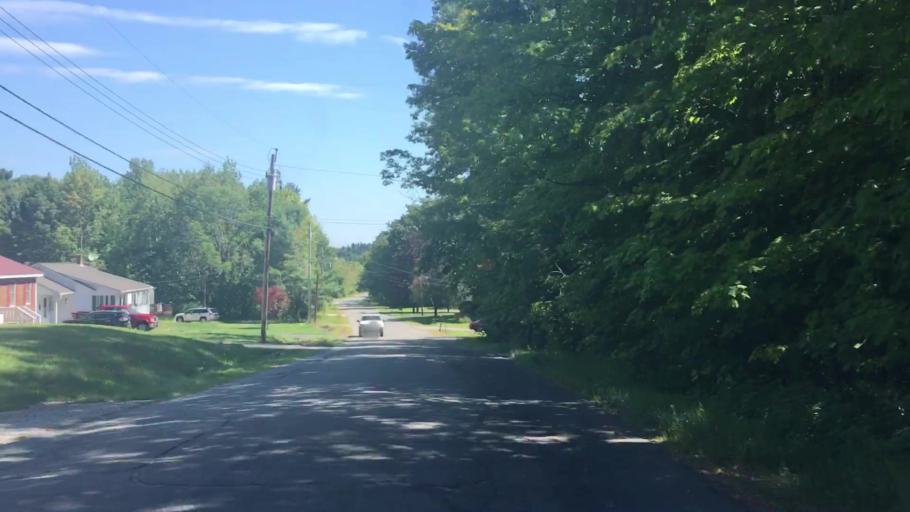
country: US
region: Maine
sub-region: Androscoggin County
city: Sabattus
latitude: 44.1181
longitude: -70.1028
